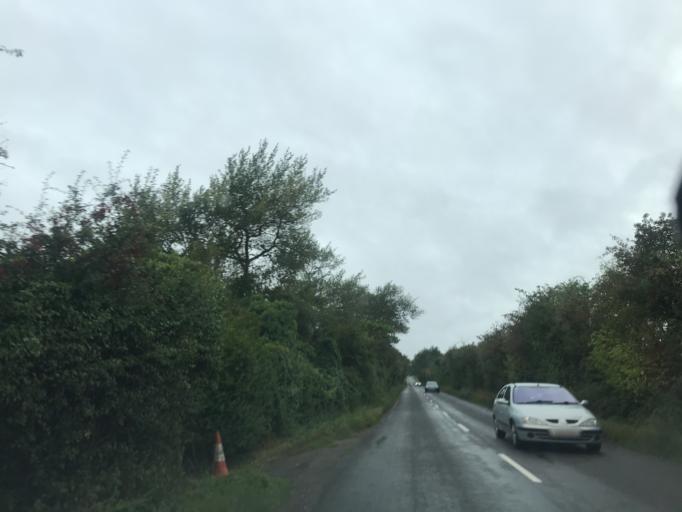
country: GB
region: England
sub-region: Buckinghamshire
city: Haddenham
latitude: 51.7785
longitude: -0.8987
